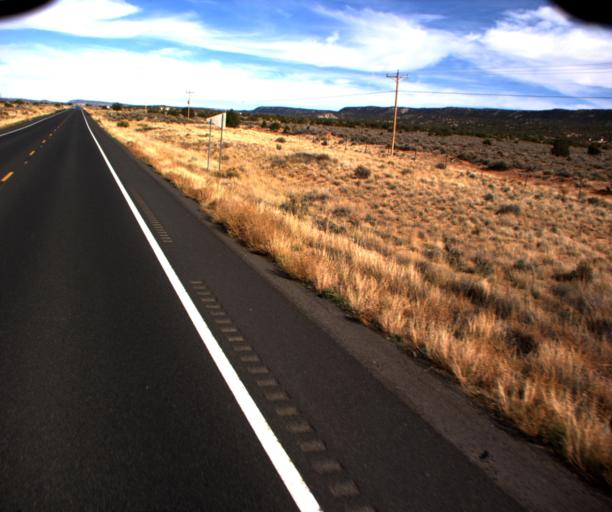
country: US
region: Arizona
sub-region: Navajo County
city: Kayenta
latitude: 36.5030
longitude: -110.6141
